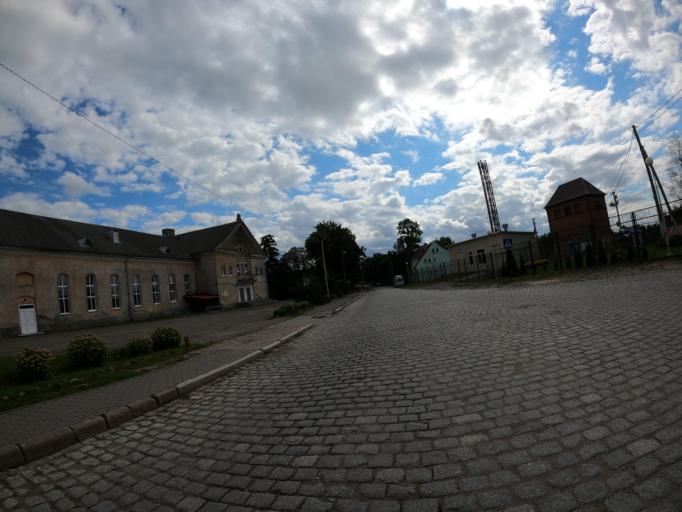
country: RU
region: Kaliningrad
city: Zheleznodorozhnyy
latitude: 54.3587
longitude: 21.3065
